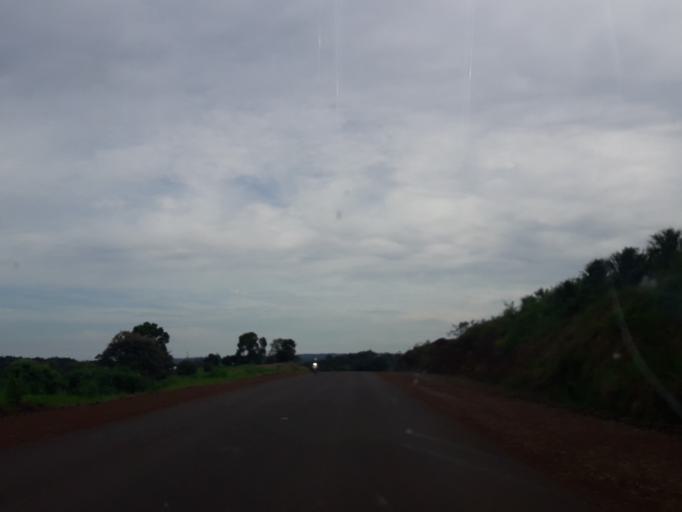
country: AR
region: Misiones
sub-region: Departamento de San Pedro
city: San Pedro
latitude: -26.5222
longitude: -53.9396
